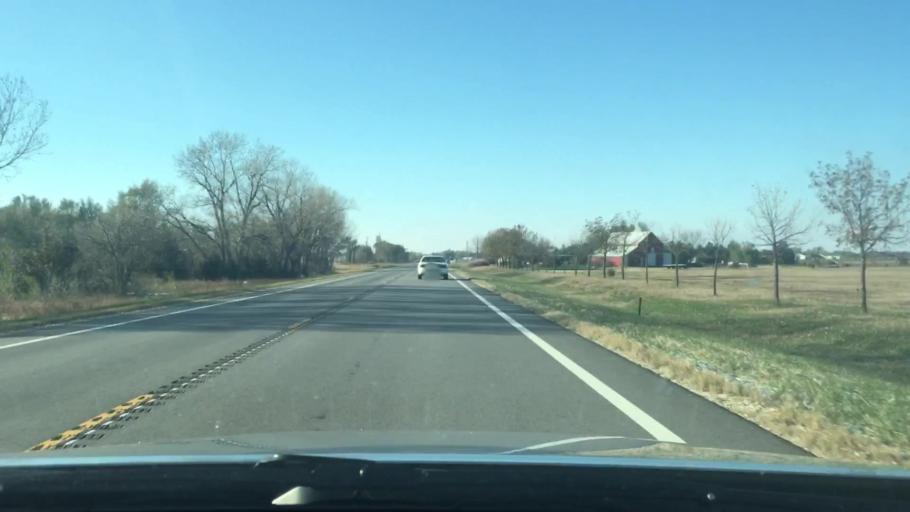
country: US
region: Kansas
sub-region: Reno County
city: Nickerson
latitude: 38.1353
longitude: -98.0663
